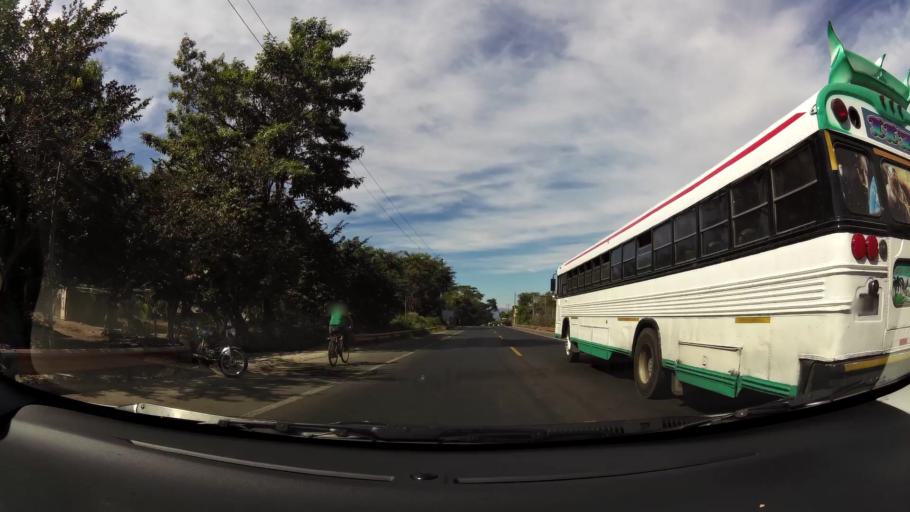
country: SV
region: San Salvador
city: Guazapa
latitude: 13.9142
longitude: -89.1825
